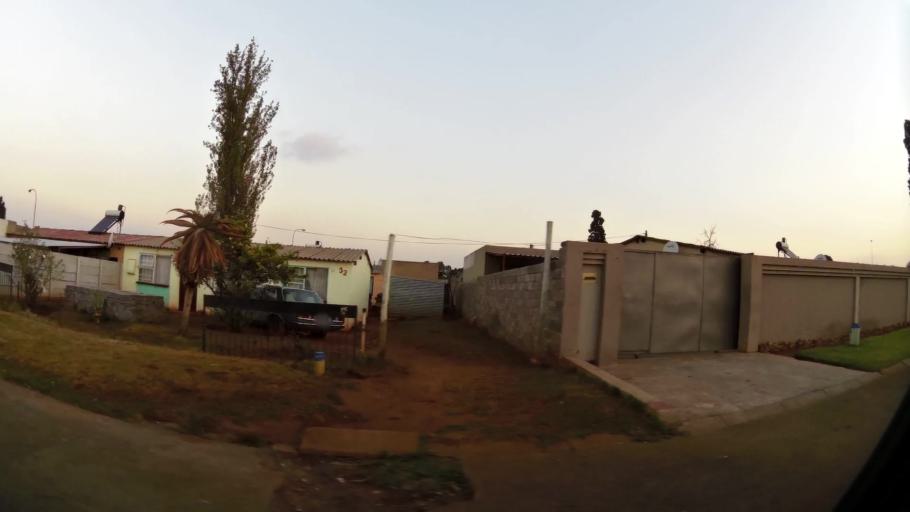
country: ZA
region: Gauteng
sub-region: City of Johannesburg Metropolitan Municipality
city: Soweto
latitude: -26.2878
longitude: 27.8806
